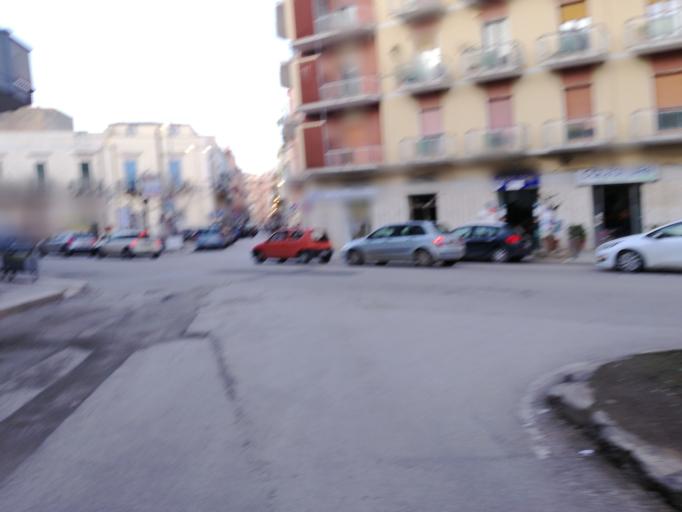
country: IT
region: Apulia
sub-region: Provincia di Bari
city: Corato
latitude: 41.1497
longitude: 16.4088
